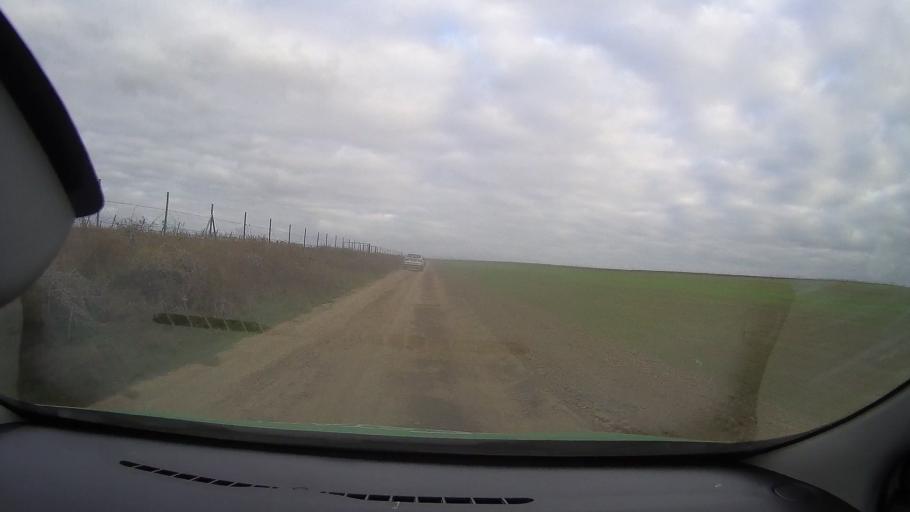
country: RO
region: Tulcea
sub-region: Comuna Jurilovca
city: Jurilovca
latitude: 44.7673
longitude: 28.9068
